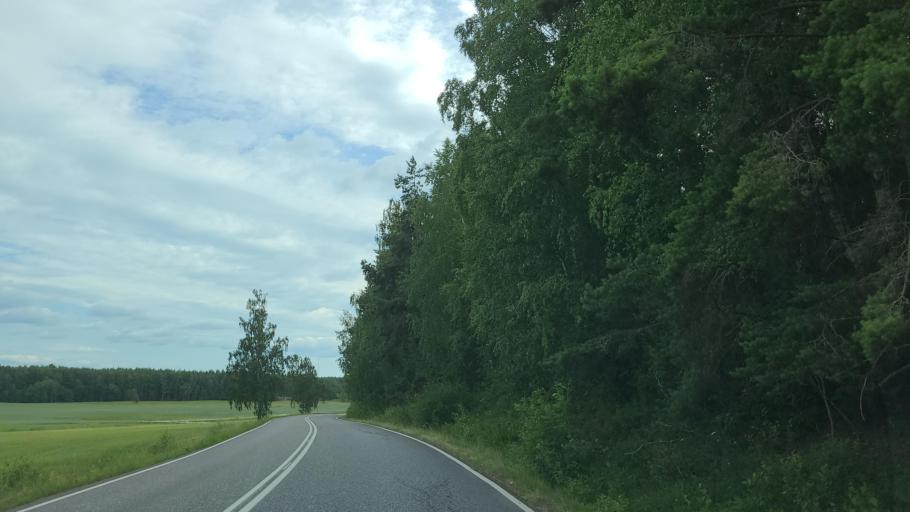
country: FI
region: Varsinais-Suomi
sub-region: Turku
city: Rymaettylae
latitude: 60.3530
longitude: 21.9585
